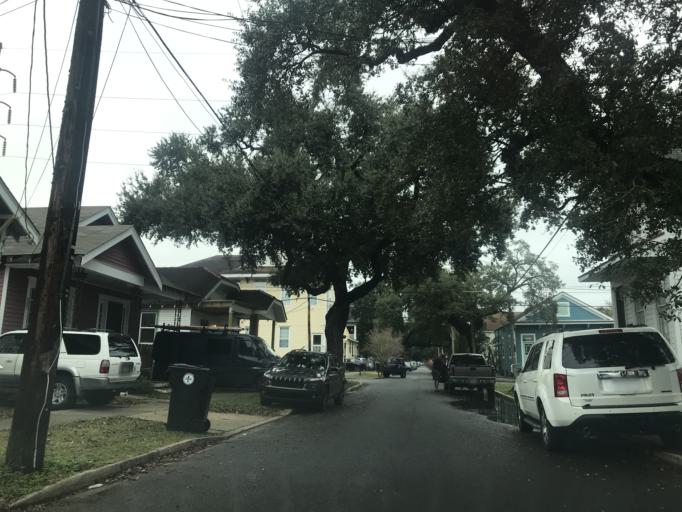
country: US
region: Louisiana
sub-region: Orleans Parish
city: New Orleans
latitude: 29.9731
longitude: -90.1075
